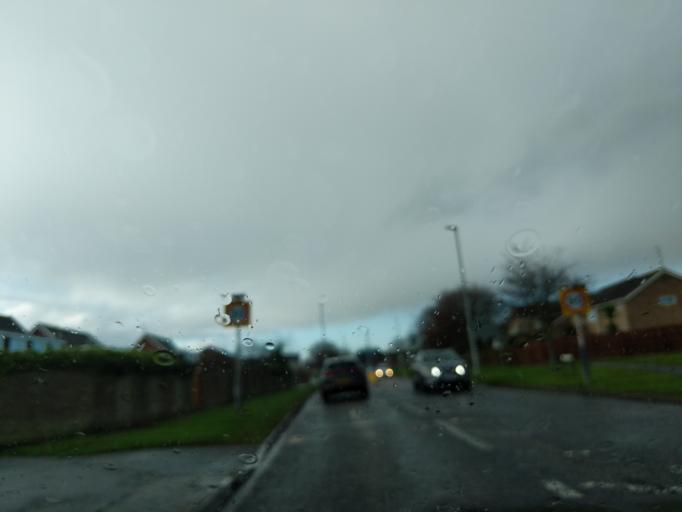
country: GB
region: England
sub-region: Northumberland
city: Blyth
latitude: 55.1148
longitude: -1.5071
